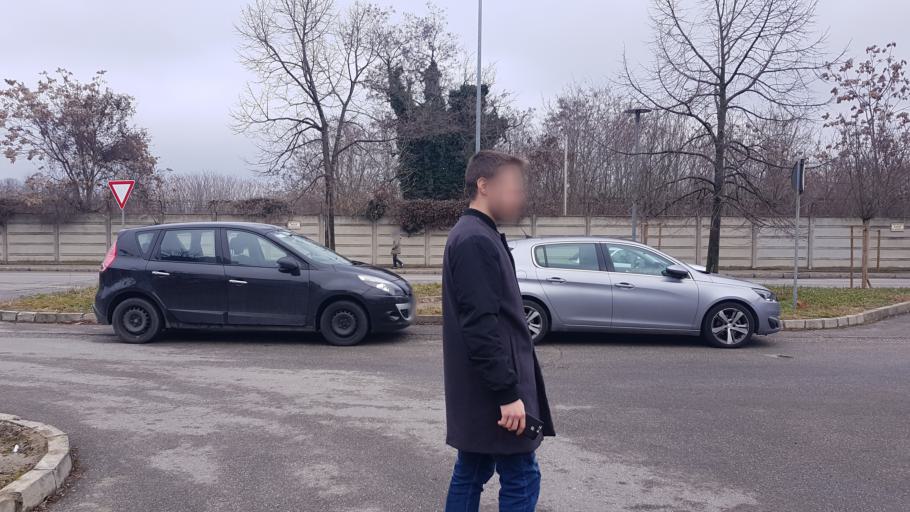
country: IT
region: Emilia-Romagna
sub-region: Provincia di Bologna
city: Bologna
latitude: 44.5087
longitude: 11.3064
